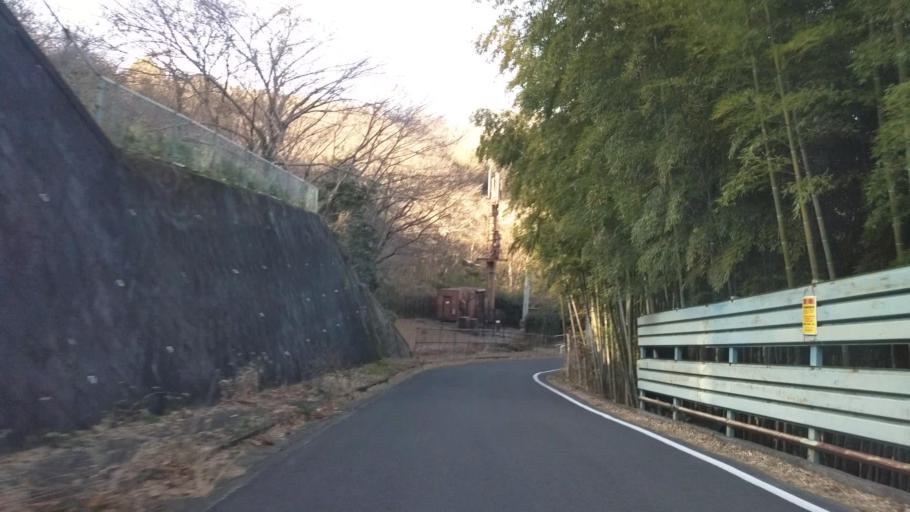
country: JP
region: Kanagawa
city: Hadano
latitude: 35.3691
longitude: 139.2493
